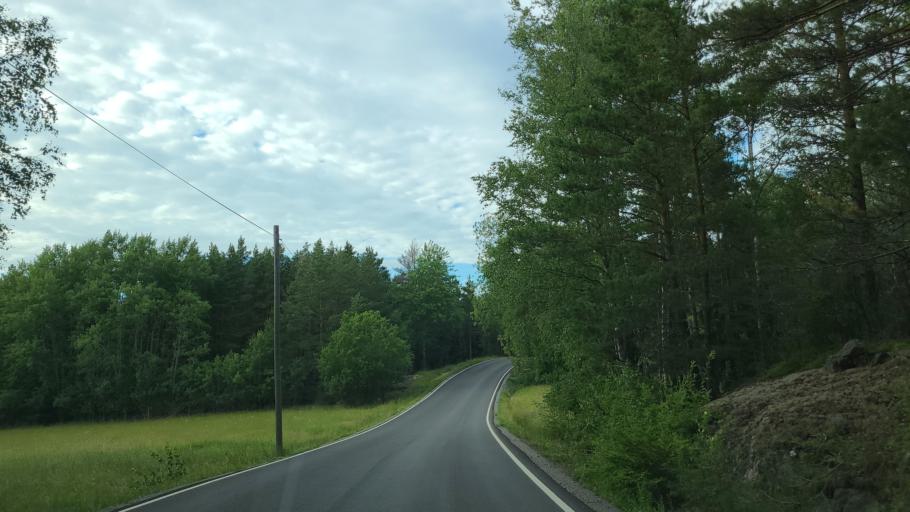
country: FI
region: Varsinais-Suomi
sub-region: Turku
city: Rymaettylae
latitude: 60.3222
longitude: 21.9560
